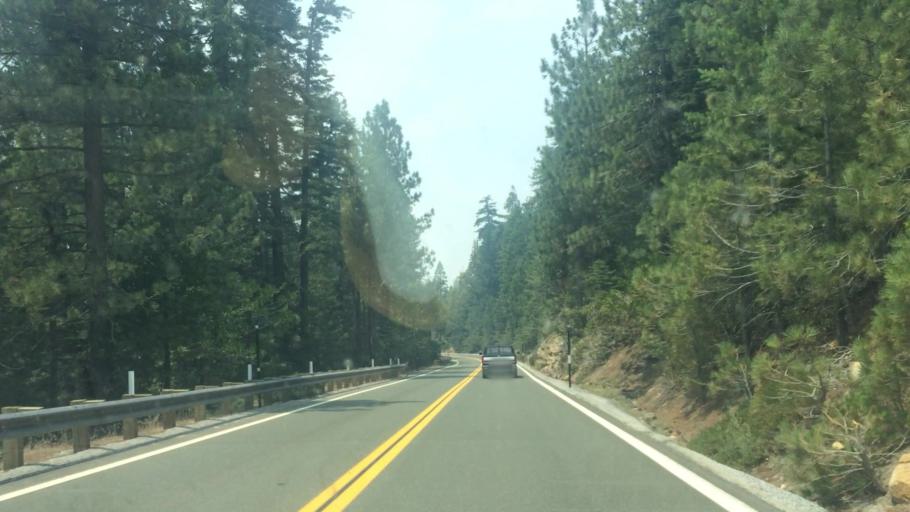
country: US
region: California
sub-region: Amador County
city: Pioneer
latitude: 38.5443
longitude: -120.3293
